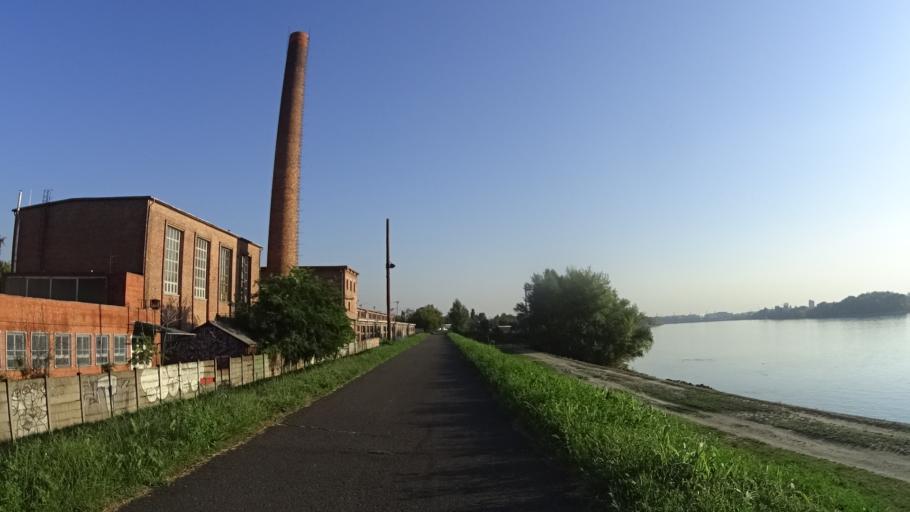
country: HU
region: Budapest
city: Budapest XXII. keruelet
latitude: 47.4467
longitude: 19.0496
